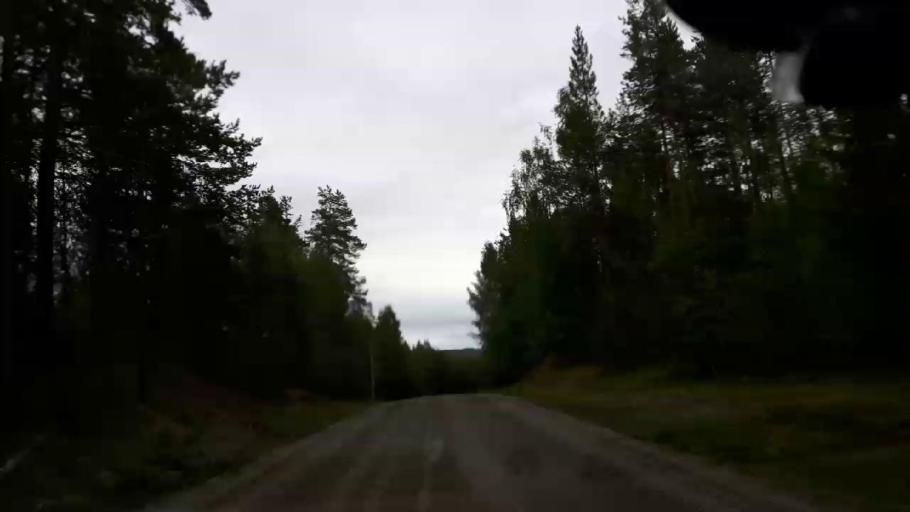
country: SE
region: Jaemtland
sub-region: Braecke Kommun
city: Braecke
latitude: 62.9113
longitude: 15.5864
